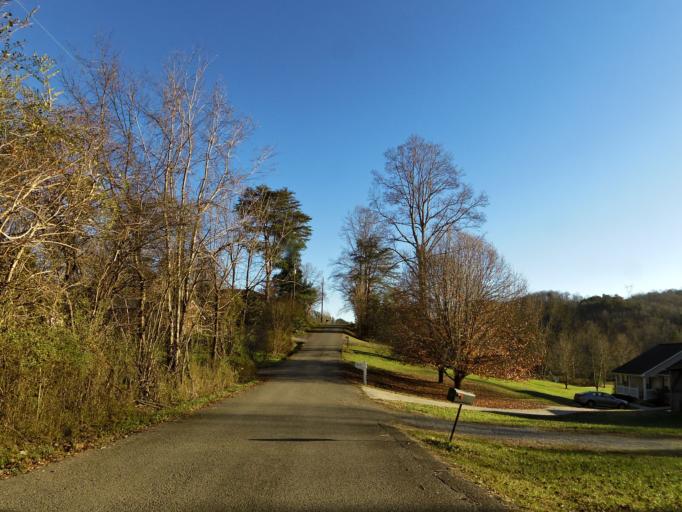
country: US
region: Tennessee
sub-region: Anderson County
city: Oak Ridge
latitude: 36.0908
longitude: -84.2392
